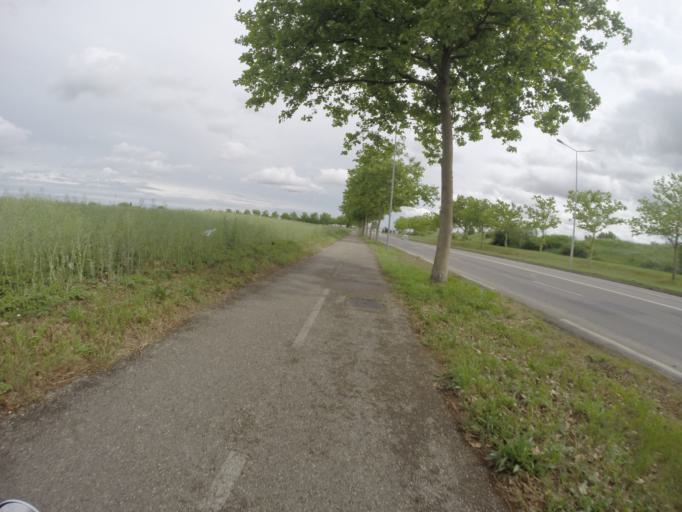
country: FR
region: Rhone-Alpes
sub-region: Departement du Rhone
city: Bron
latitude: 45.7409
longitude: 4.9366
